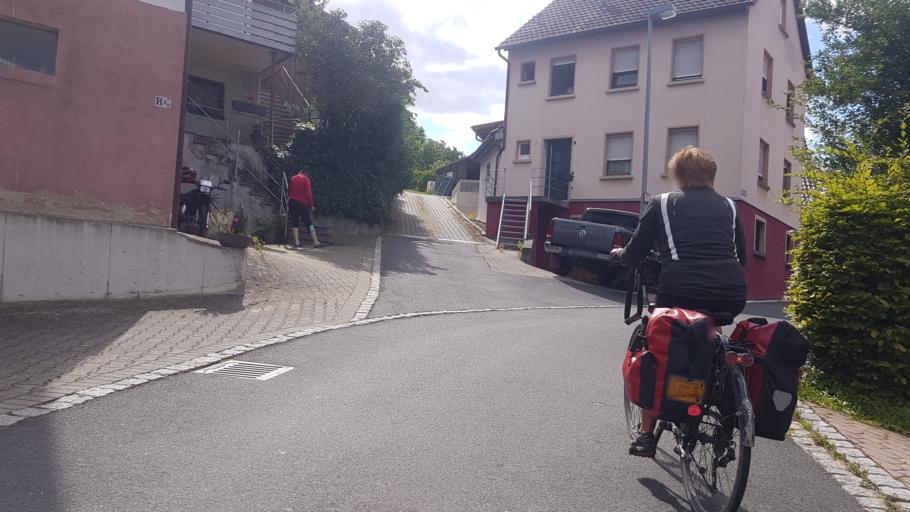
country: DE
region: Baden-Wuerttemberg
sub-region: Regierungsbezirk Stuttgart
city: Forchtenberg
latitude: 49.3424
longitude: 9.5599
